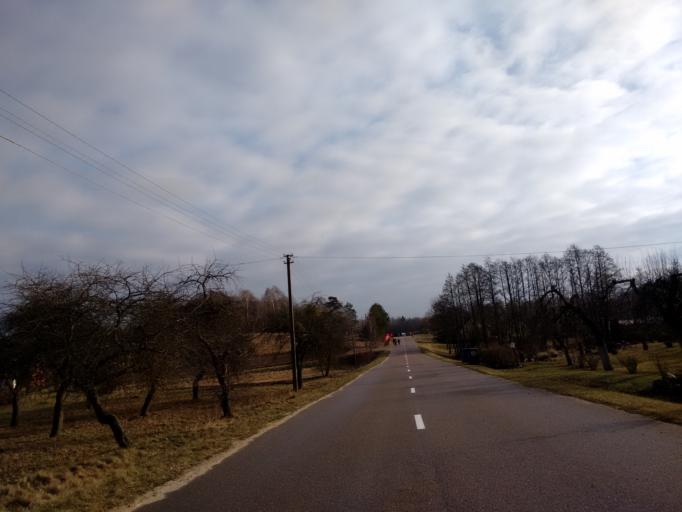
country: LT
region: Alytaus apskritis
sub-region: Alytus
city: Alytus
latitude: 54.2465
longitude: 23.9289
